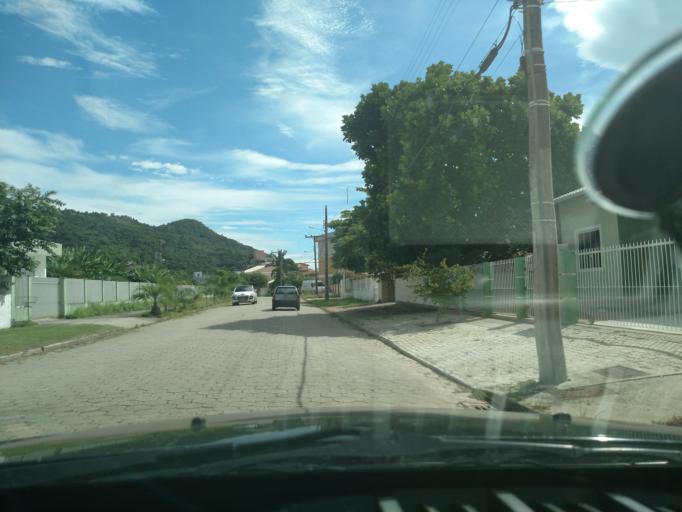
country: BR
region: Santa Catarina
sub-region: Tijucas
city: Tijucas
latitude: -27.3223
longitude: -48.5435
